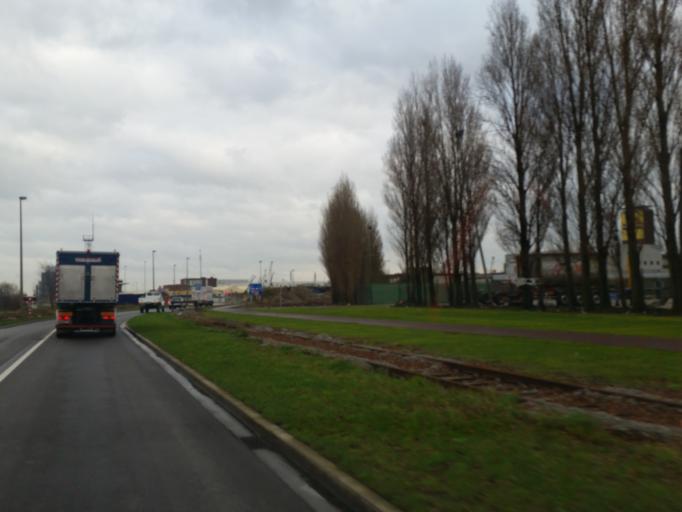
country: BE
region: Flanders
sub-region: Provincie Antwerpen
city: Antwerpen
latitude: 51.2650
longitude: 4.3801
